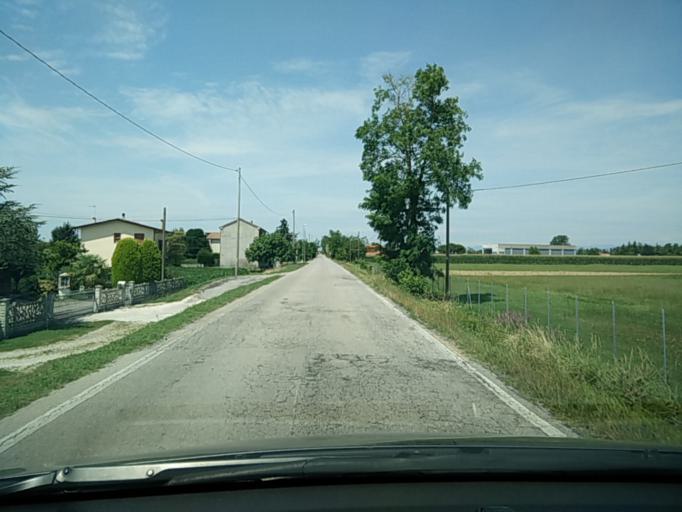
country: IT
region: Veneto
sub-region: Provincia di Venezia
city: Passarella
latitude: 45.6015
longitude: 12.5913
